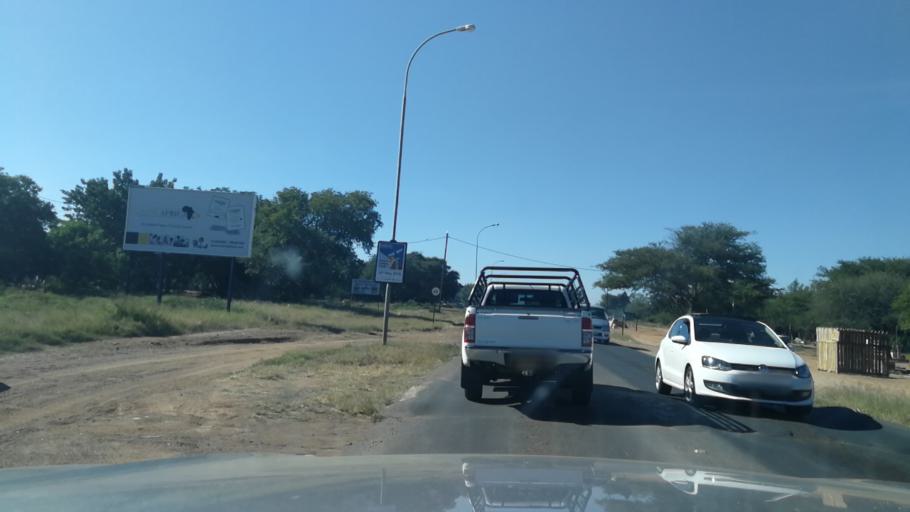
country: BW
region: South East
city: Gaborone
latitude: -24.6955
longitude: 25.8942
